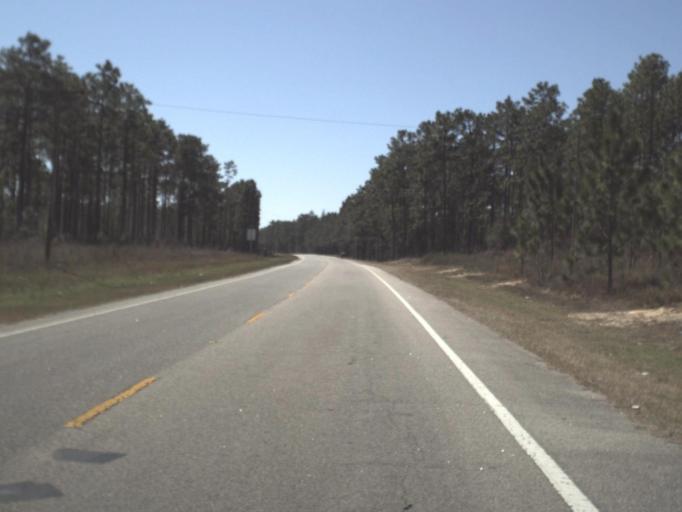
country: US
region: Florida
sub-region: Leon County
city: Woodville
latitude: 30.3434
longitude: -84.3107
